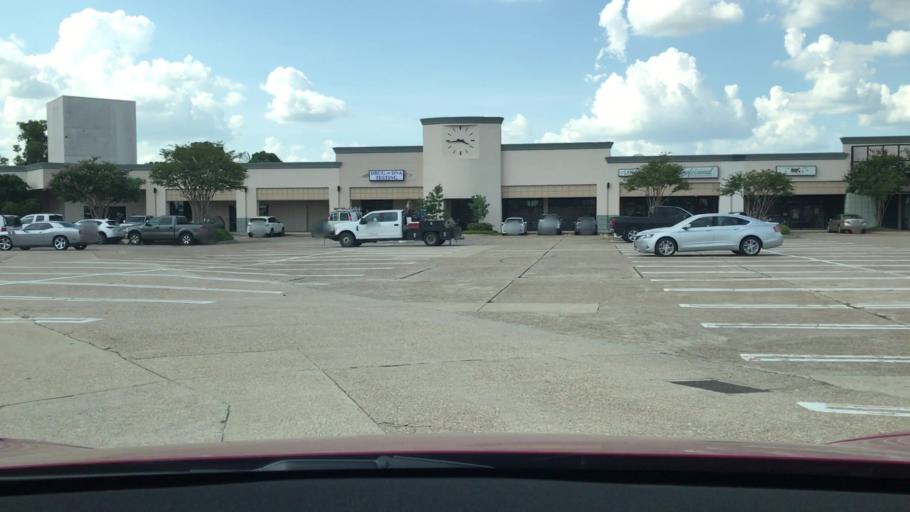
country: US
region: Louisiana
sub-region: Bossier Parish
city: Bossier City
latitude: 32.5161
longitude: -93.7181
